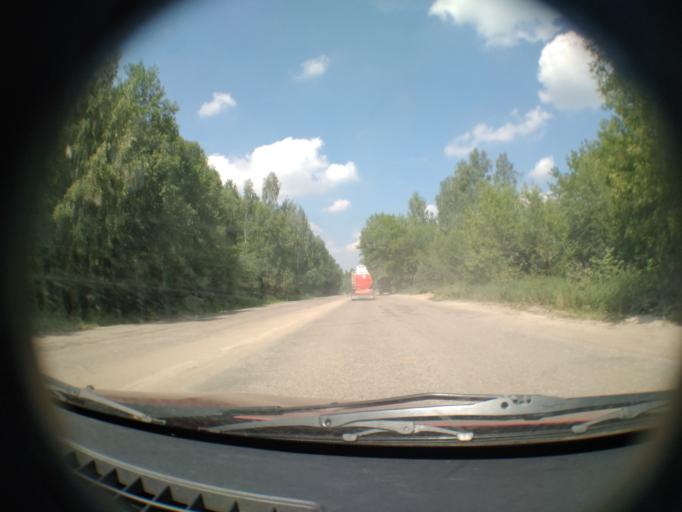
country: RU
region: Moskovskaya
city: Yakovlevskoye
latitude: 55.4298
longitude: 37.8952
